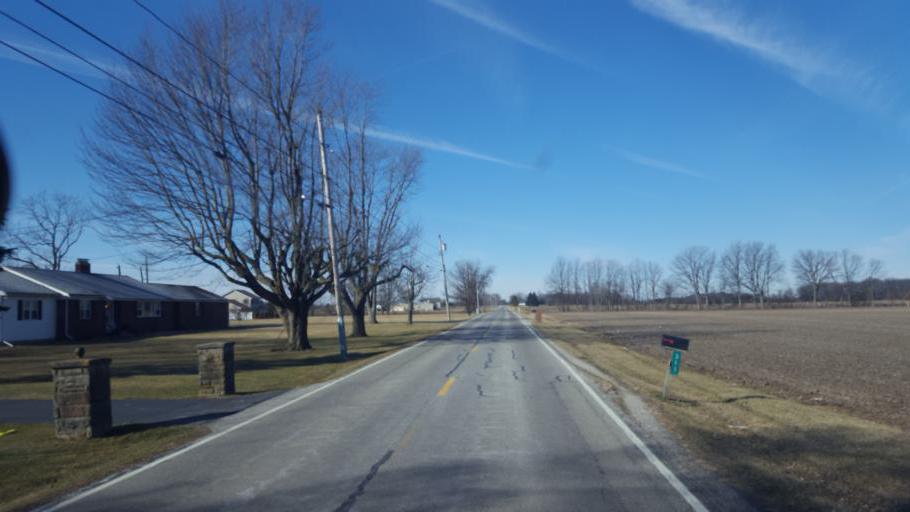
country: US
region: Ohio
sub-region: Marion County
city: Marion
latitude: 40.5349
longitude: -83.1145
